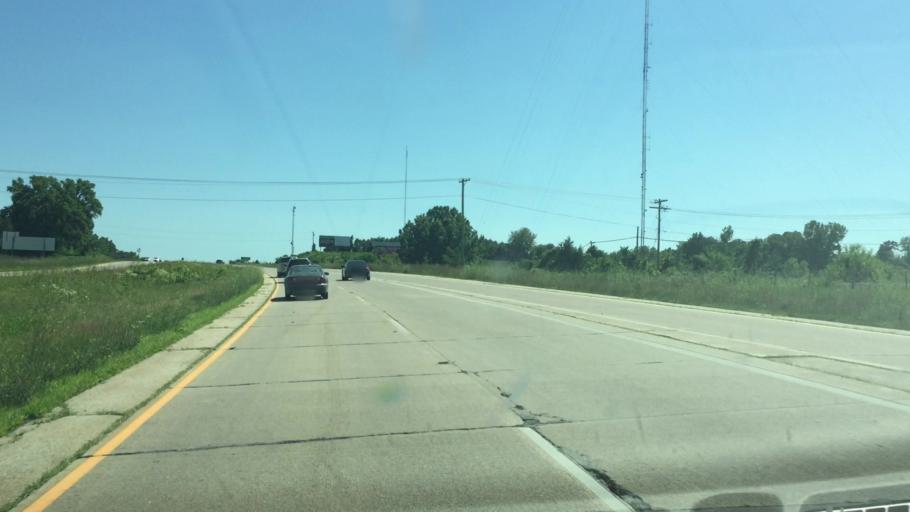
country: US
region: Illinois
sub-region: Jo Daviess County
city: East Dubuque
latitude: 42.5323
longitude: -90.6130
